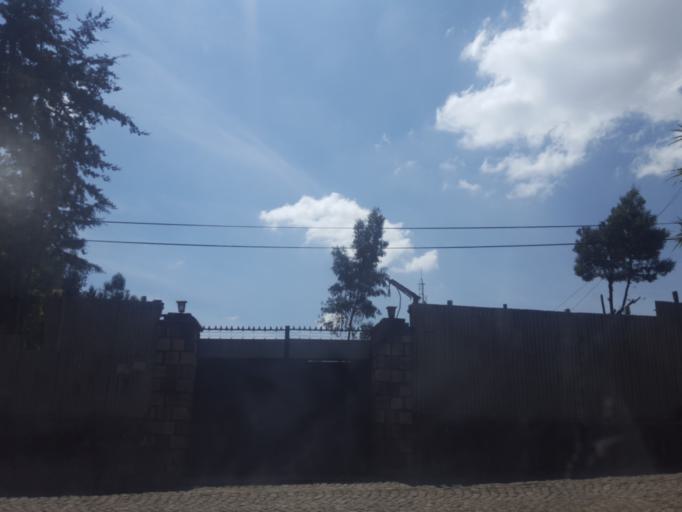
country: ET
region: Adis Abeba
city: Addis Ababa
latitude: 9.0514
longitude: 38.7309
